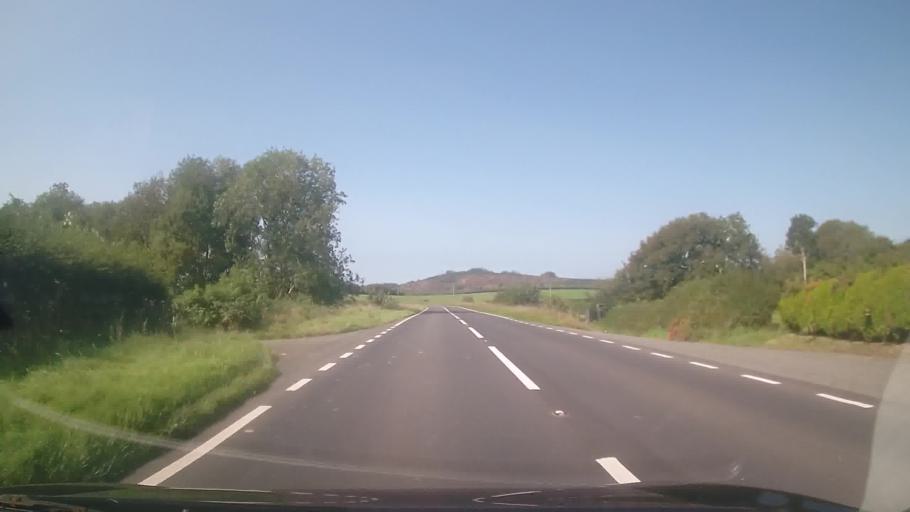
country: GB
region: Wales
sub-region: Sir Powys
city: Builth Wells
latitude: 52.1390
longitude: -3.5155
